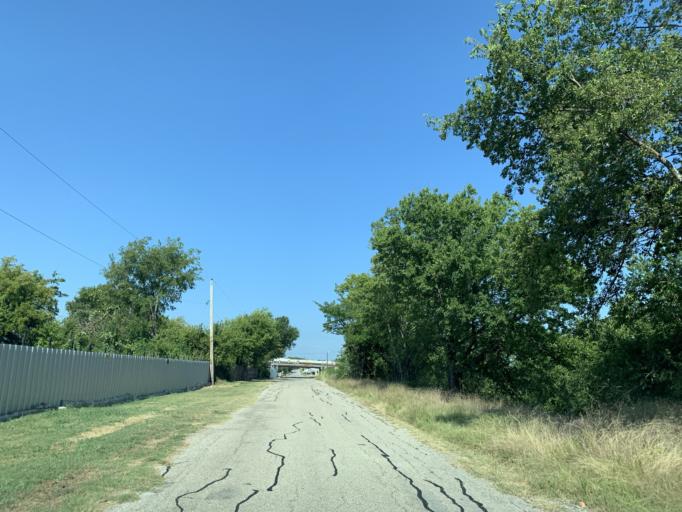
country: US
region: Texas
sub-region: Tarrant County
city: Lakeside
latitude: 32.8380
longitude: -97.4888
